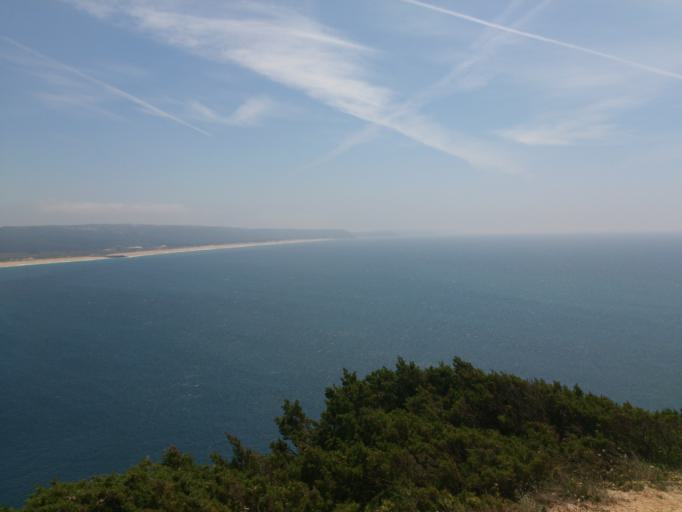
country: PT
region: Leiria
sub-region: Nazare
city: Nazare
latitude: 39.6044
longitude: -9.0805
